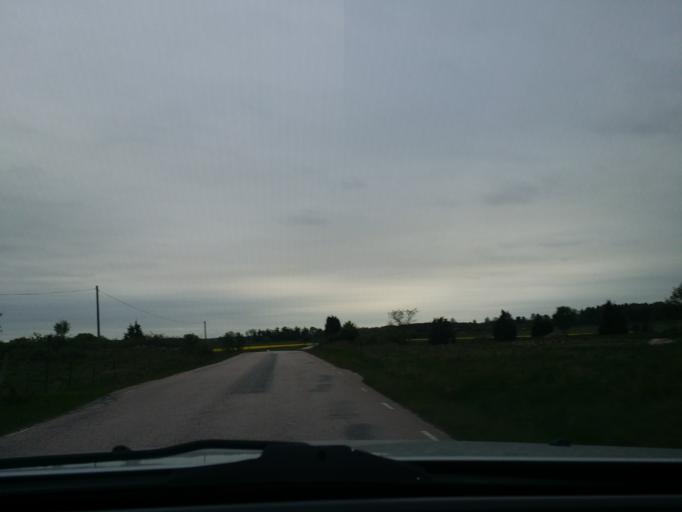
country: SE
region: Vaestmanland
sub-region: Hallstahammars Kommun
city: Kolback
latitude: 59.5431
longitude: 16.3087
